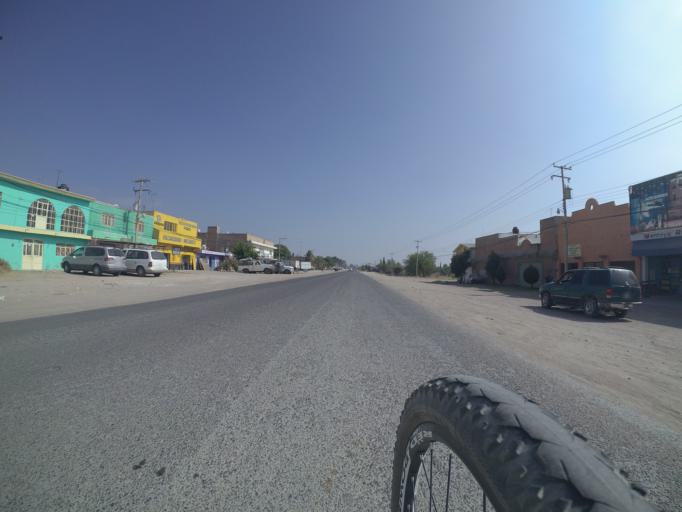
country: MX
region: Aguascalientes
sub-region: Jesus Maria
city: Jesus Maria
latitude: 21.9682
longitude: -102.3415
